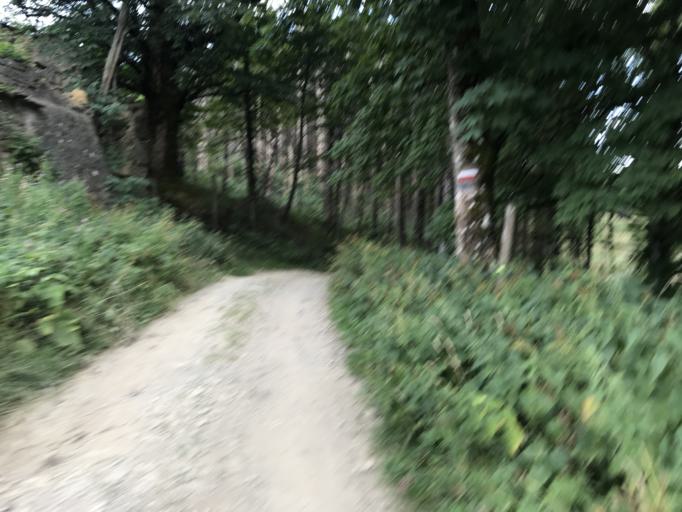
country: IT
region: Emilia-Romagna
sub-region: Provincia di Bologna
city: San Benedetto Val di Sambro
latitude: 44.1525
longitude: 11.2626
